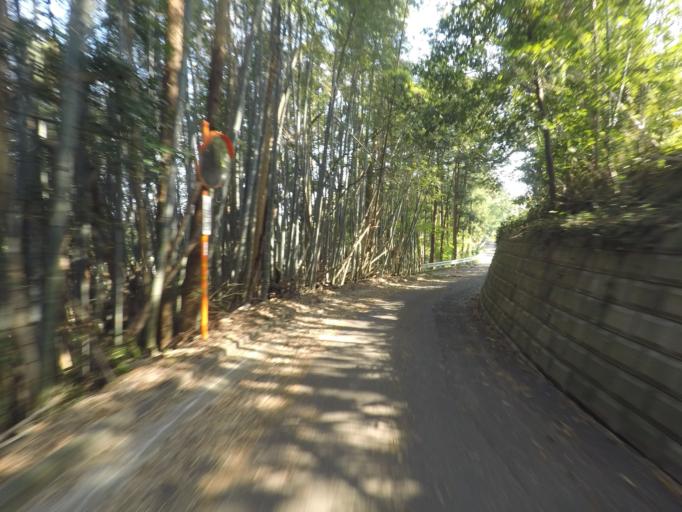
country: JP
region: Ibaraki
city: Itako
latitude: 36.0539
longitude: 140.4484
